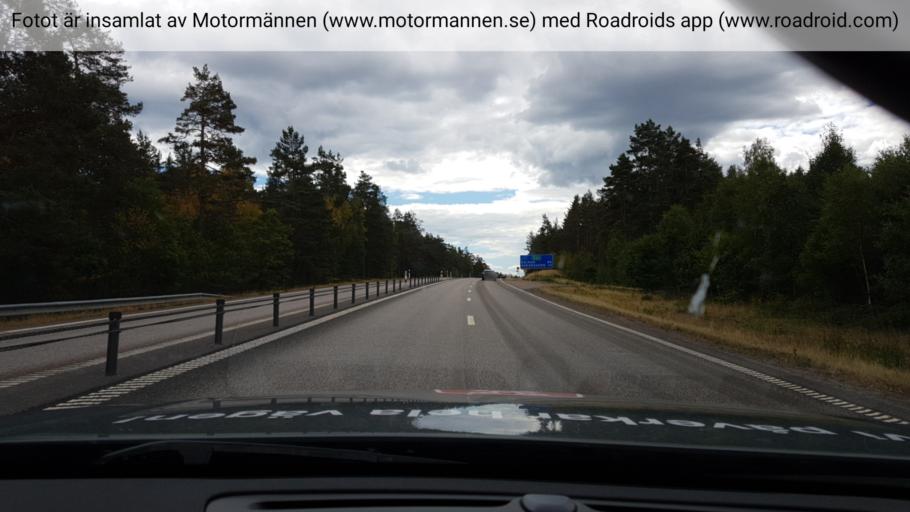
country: SE
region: Kalmar
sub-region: Oskarshamns Kommun
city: Oskarshamn
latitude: 57.3690
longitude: 16.4923
